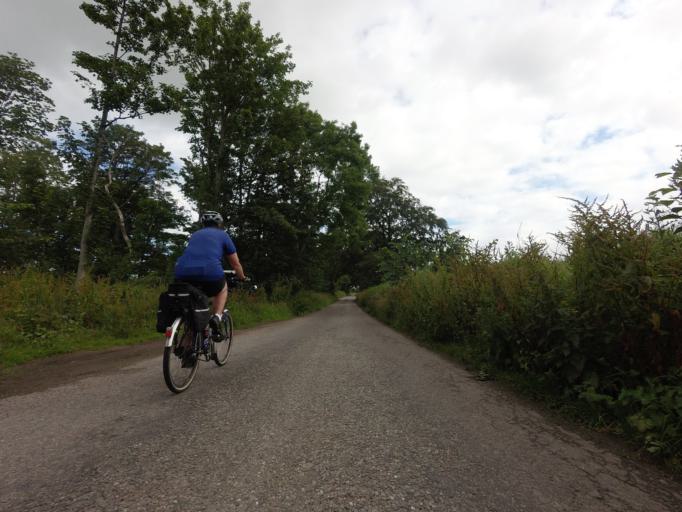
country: GB
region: Scotland
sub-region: Moray
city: Lhanbryd
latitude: 57.6424
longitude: -3.2623
